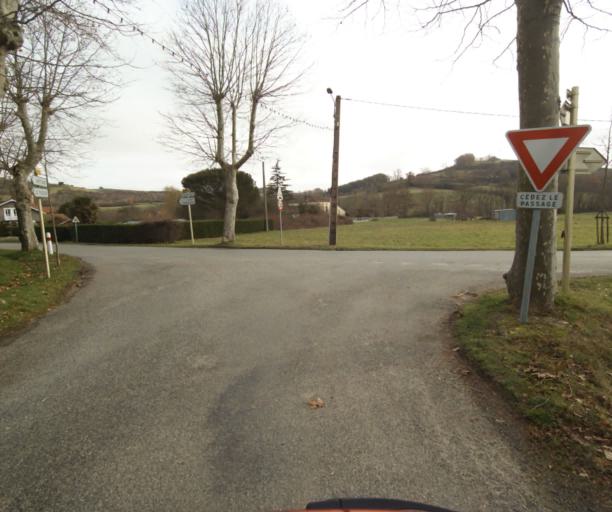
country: FR
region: Midi-Pyrenees
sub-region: Departement de la Haute-Garonne
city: Gaillac-Toulza
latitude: 43.1681
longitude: 1.4948
